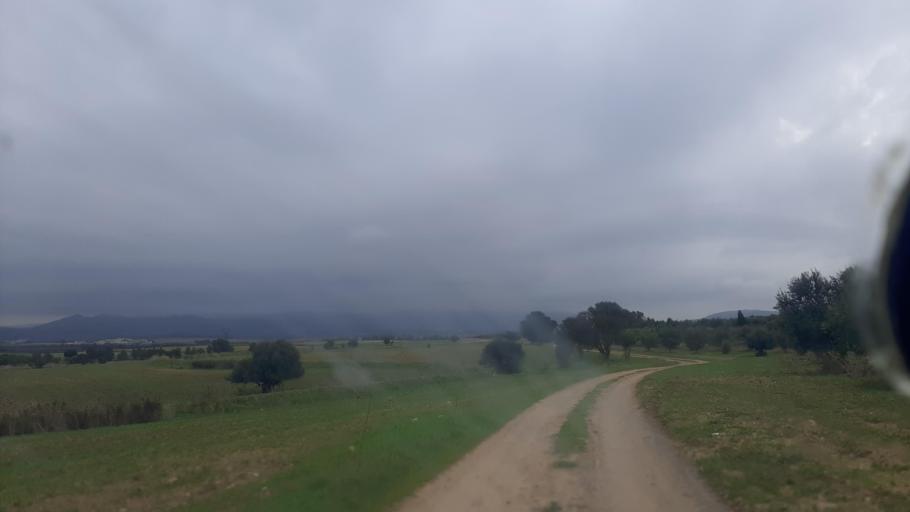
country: TN
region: Tunis
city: La Sebala du Mornag
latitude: 36.5735
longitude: 10.2937
